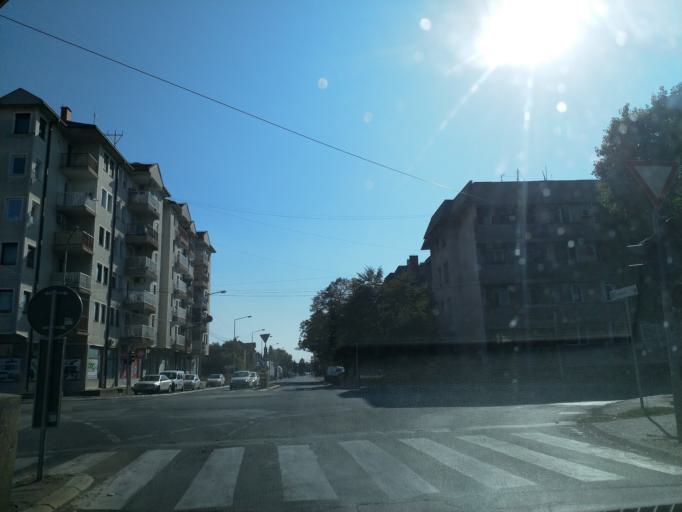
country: RS
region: Central Serbia
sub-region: Pomoravski Okrug
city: Paracin
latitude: 43.8608
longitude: 21.4218
